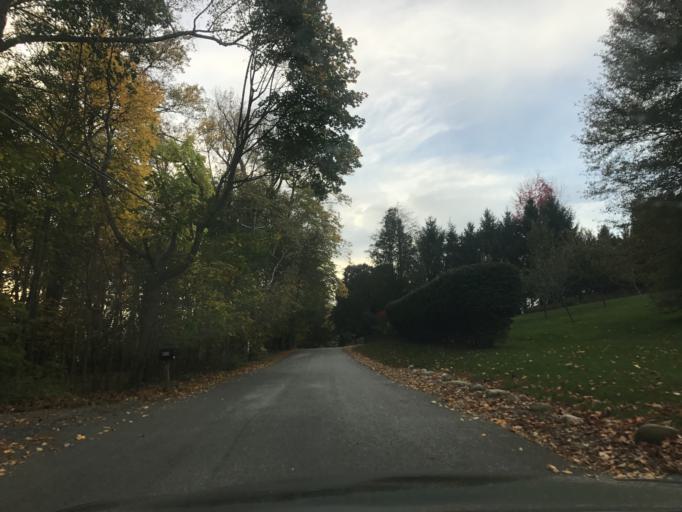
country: US
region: Maryland
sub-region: Baltimore County
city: Lutherville
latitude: 39.3931
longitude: -76.6332
